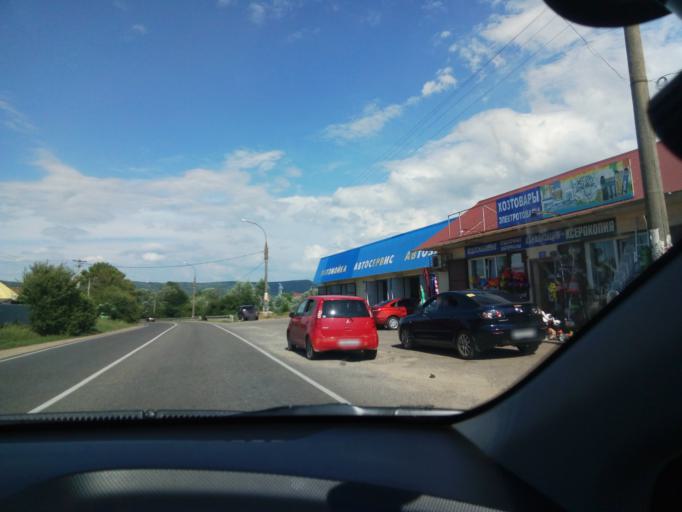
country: RU
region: Krasnodarskiy
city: Apsheronsk
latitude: 44.4657
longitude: 39.7117
